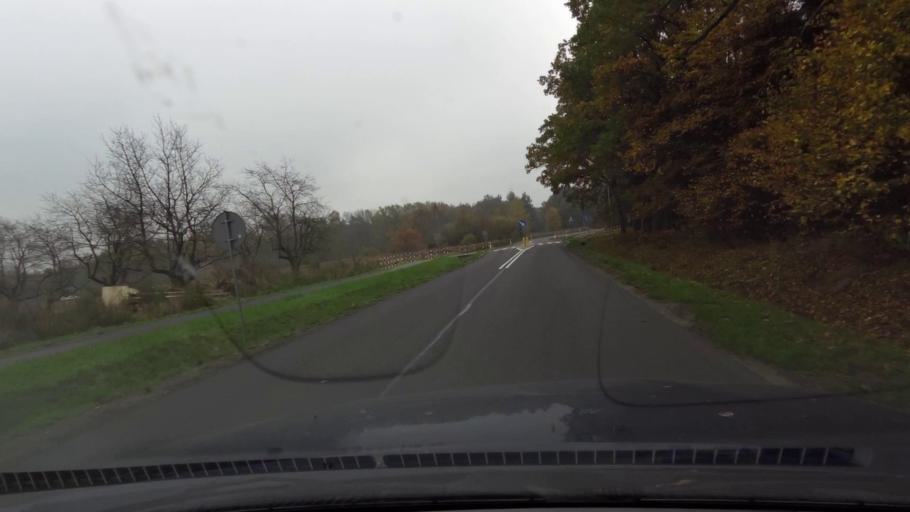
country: PL
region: West Pomeranian Voivodeship
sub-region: Powiat goleniowski
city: Goleniow
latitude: 53.5758
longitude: 14.8011
